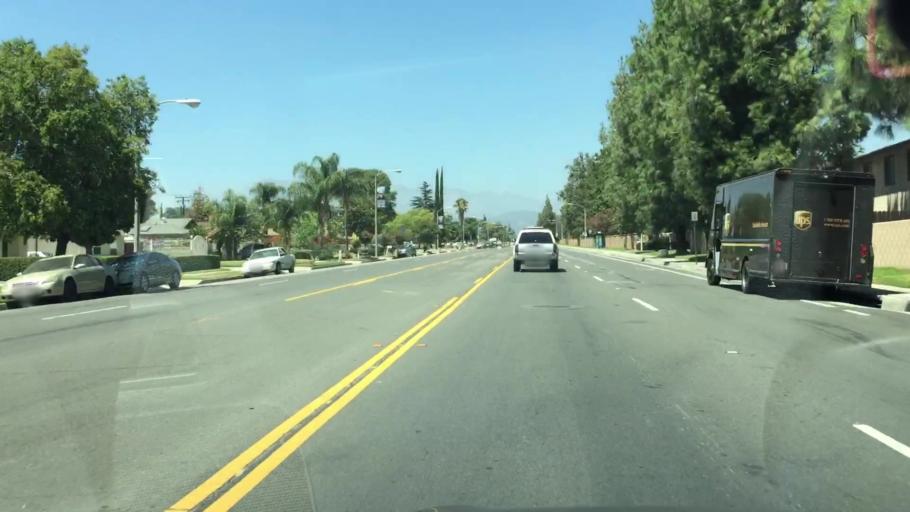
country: US
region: California
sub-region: San Bernardino County
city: Muscoy
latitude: 34.1696
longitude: -117.3167
